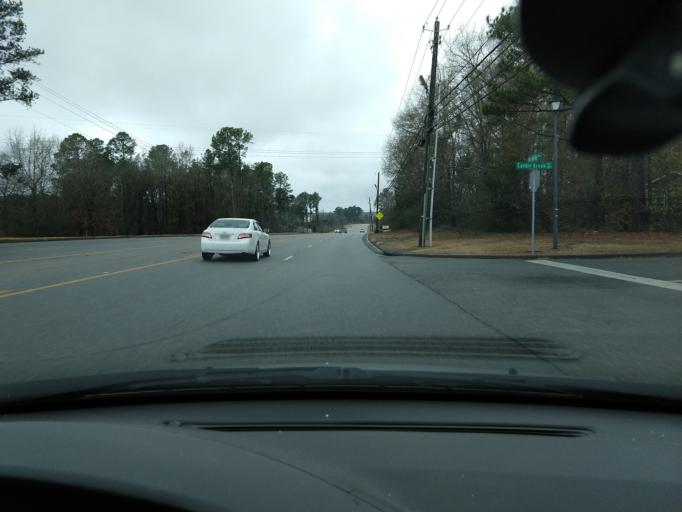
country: US
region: Alabama
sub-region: Houston County
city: Dothan
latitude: 31.2636
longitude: -85.4207
